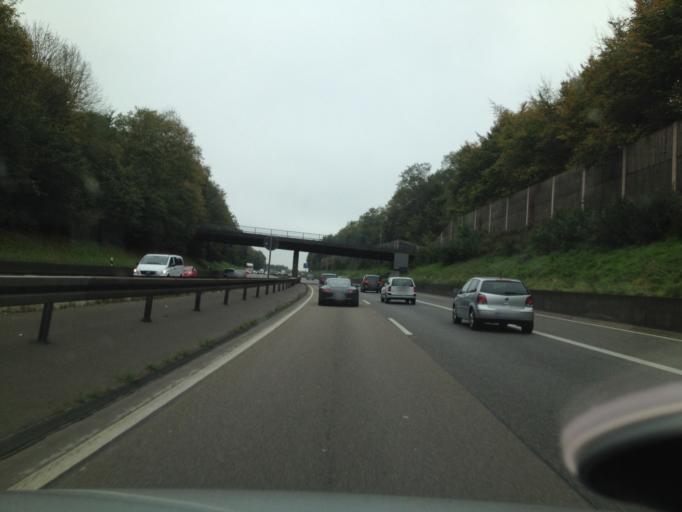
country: DE
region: North Rhine-Westphalia
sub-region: Regierungsbezirk Koln
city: Rath
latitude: 50.9510
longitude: 7.0852
